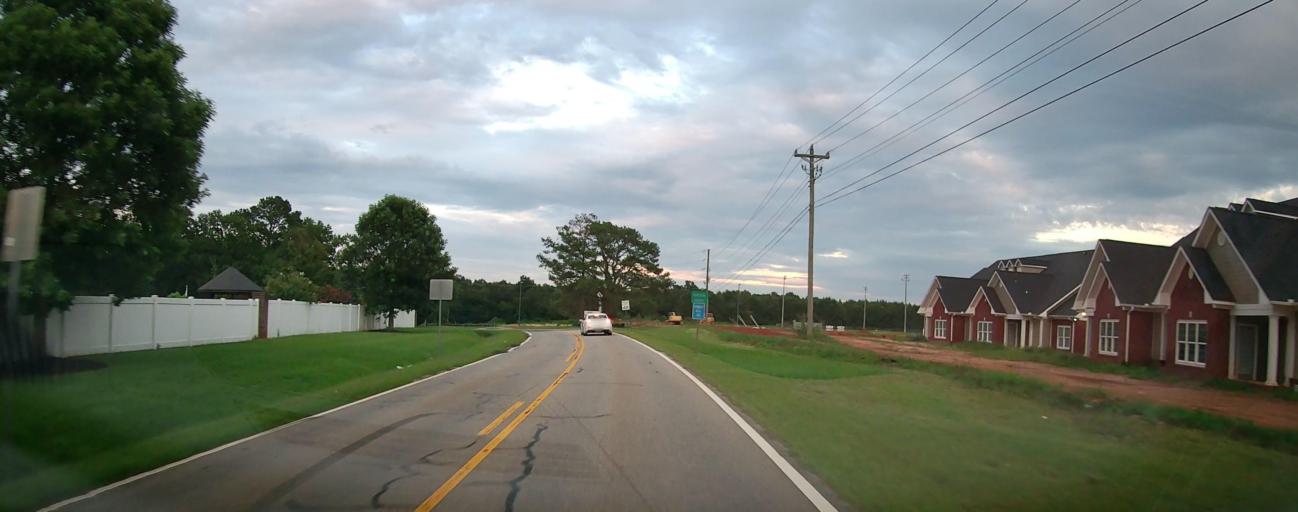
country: US
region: Georgia
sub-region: Houston County
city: Centerville
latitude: 32.6186
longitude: -83.7200
